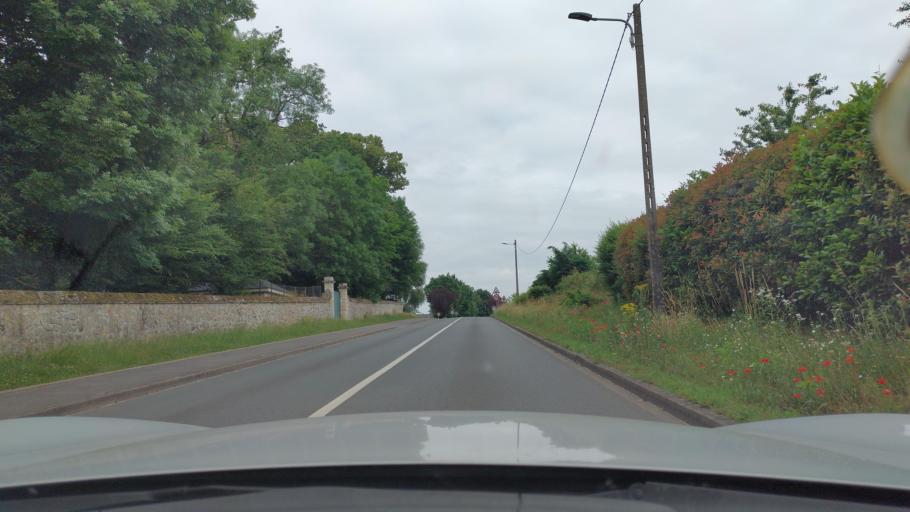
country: FR
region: Picardie
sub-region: Departement de l'Oise
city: Betz
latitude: 49.1585
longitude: 2.9512
